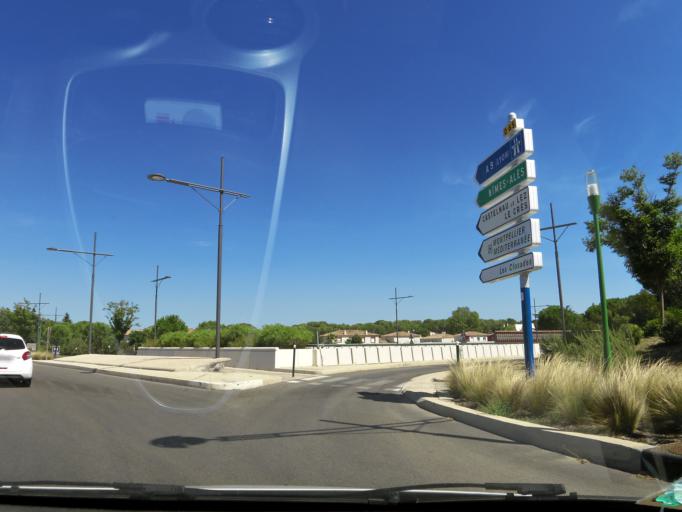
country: FR
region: Languedoc-Roussillon
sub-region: Departement de l'Herault
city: Clapiers
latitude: 43.6527
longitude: 3.8816
